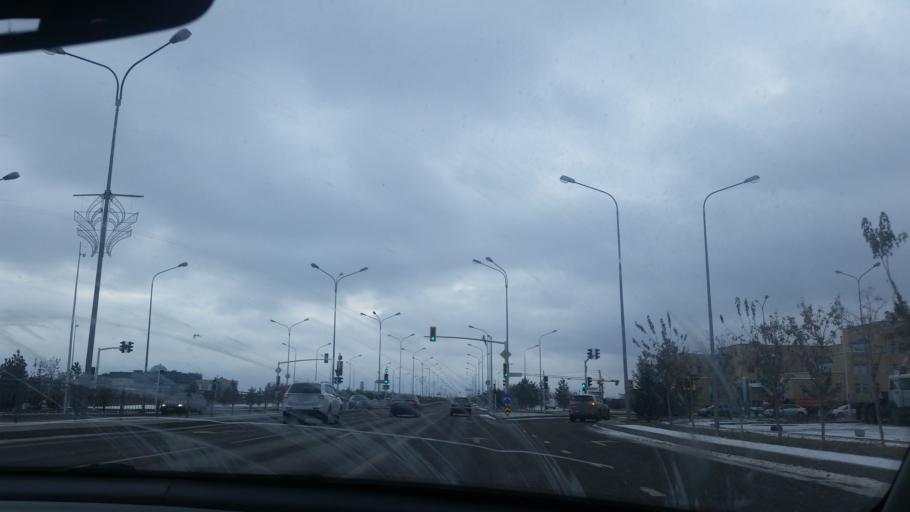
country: KZ
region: Astana Qalasy
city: Astana
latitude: 51.0842
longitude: 71.4227
